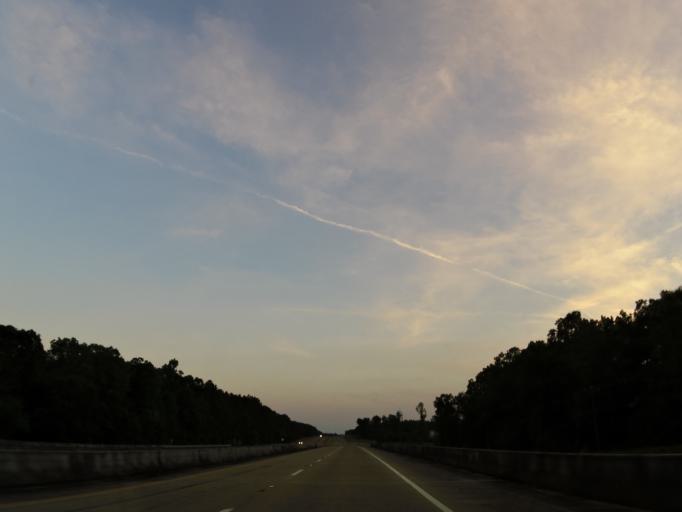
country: US
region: Mississippi
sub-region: Kemper County
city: De Kalb
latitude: 32.7576
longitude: -88.4658
